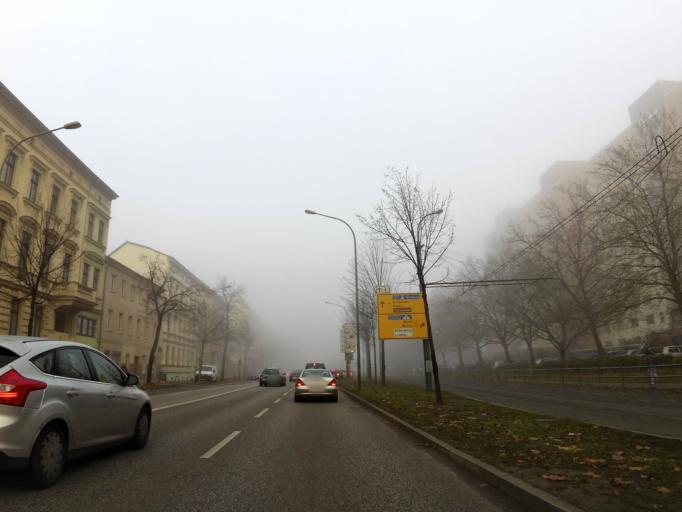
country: DE
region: Brandenburg
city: Potsdam
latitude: 52.3957
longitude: 13.0412
